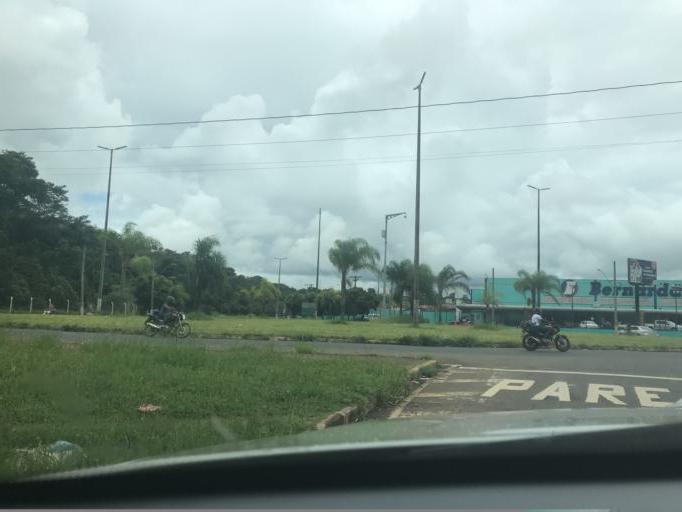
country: BR
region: Minas Gerais
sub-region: Araxa
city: Araxa
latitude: -19.5823
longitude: -46.9428
